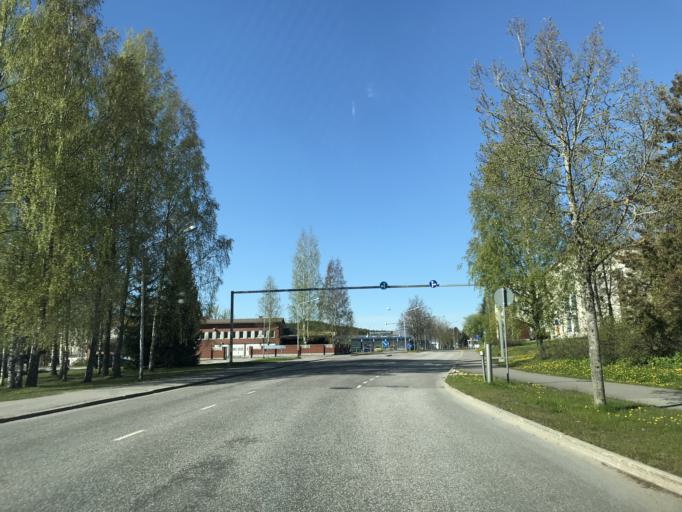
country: FI
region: Paijanne Tavastia
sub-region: Lahti
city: Orimattila
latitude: 60.8065
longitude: 25.7345
